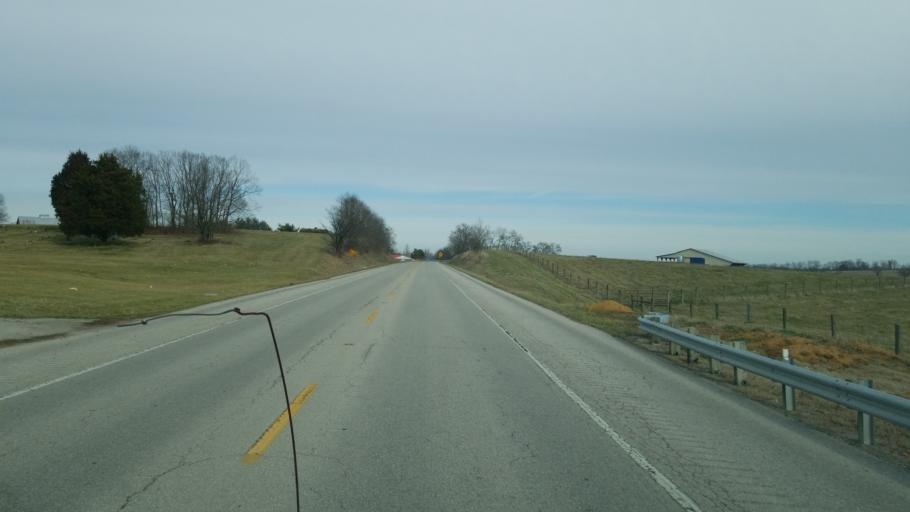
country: US
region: Kentucky
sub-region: Fleming County
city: Flemingsburg
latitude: 38.5132
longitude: -83.8420
